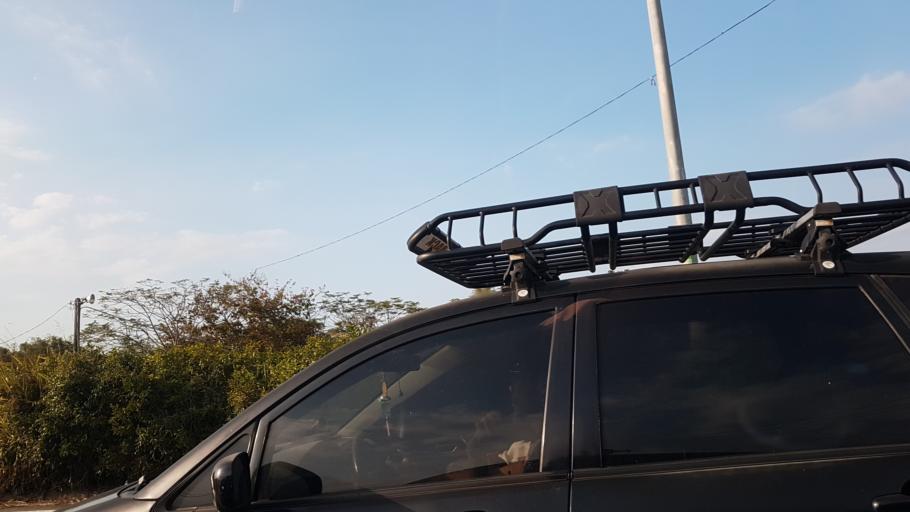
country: TW
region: Taiwan
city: Xinying
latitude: 23.3453
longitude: 120.4276
